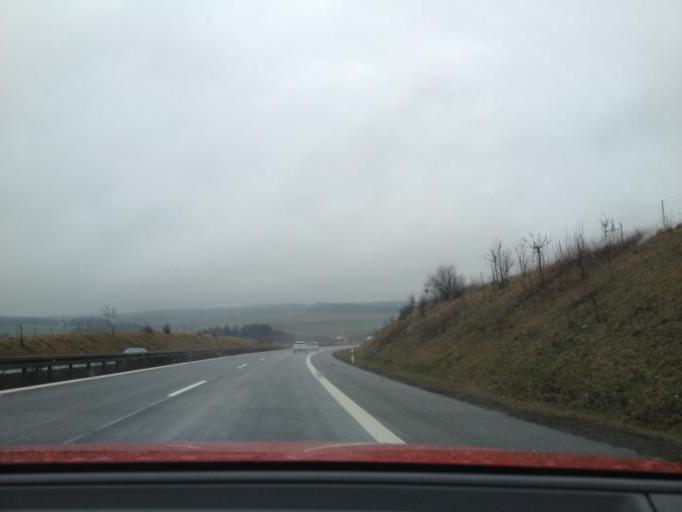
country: DE
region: Bavaria
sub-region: Upper Franconia
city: Regnitzlosau
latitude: 50.3008
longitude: 12.0272
